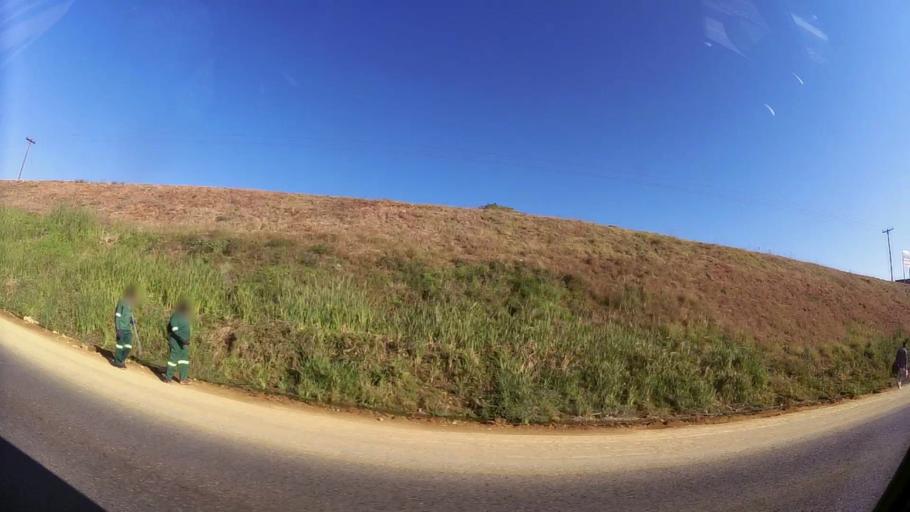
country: ZA
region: Gauteng
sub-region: City of Johannesburg Metropolitan Municipality
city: Midrand
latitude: -25.9017
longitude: 28.1025
